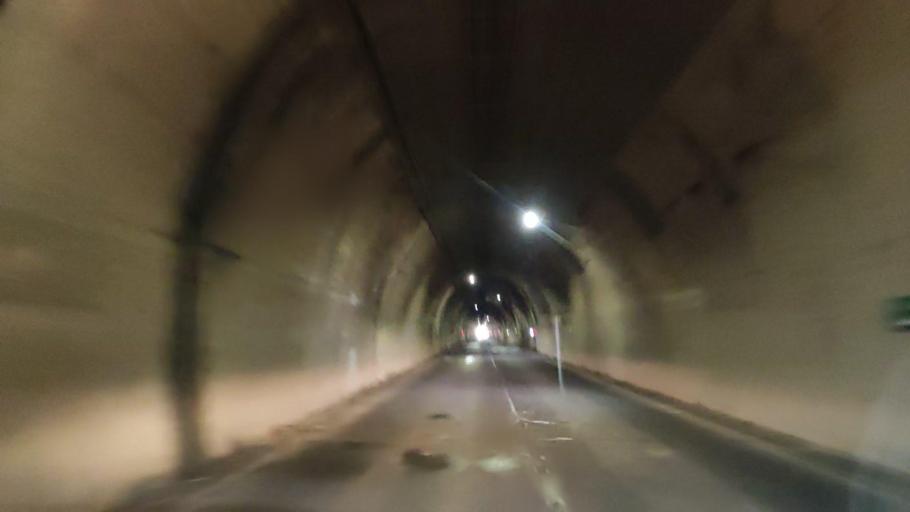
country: JP
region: Yamagata
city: Shinjo
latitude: 38.9633
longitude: 140.3546
